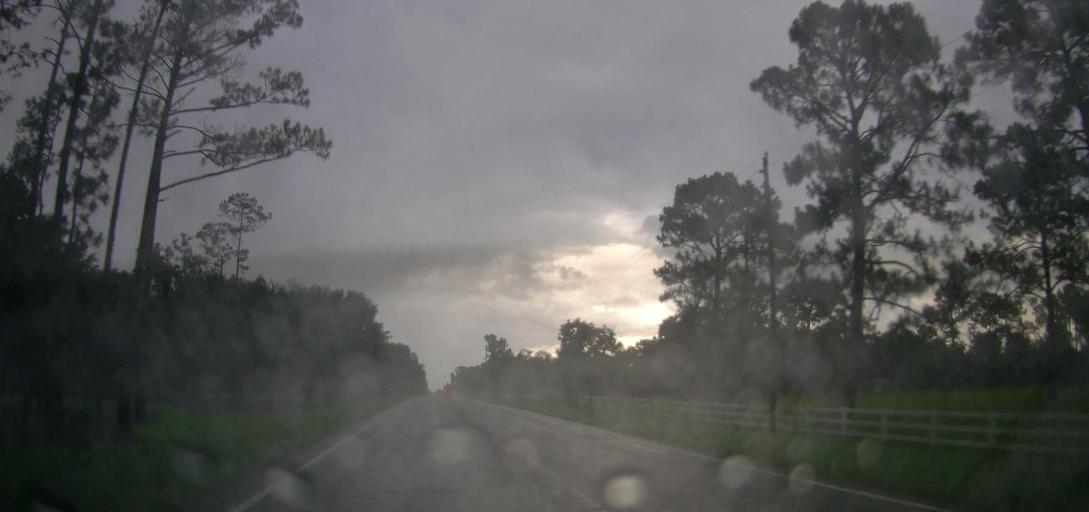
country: US
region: Georgia
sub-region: Brantley County
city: Nahunta
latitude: 31.3308
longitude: -81.7707
